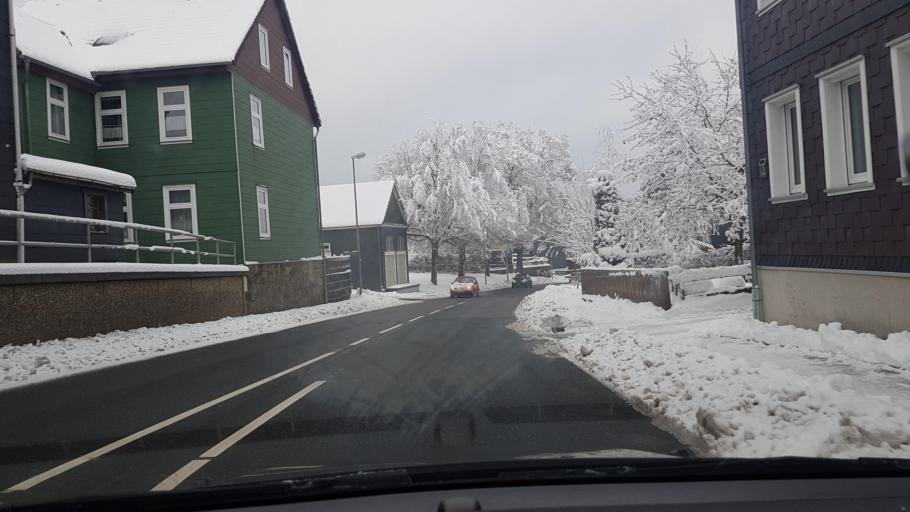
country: DE
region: Lower Saxony
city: Clausthal-Zellerfeld
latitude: 51.7992
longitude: 10.3403
